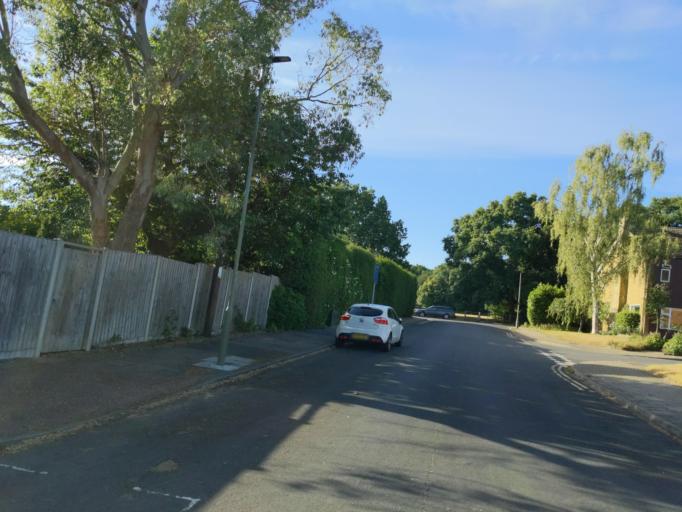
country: GB
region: England
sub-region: Greater London
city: West Wickham
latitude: 51.3747
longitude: 0.0112
